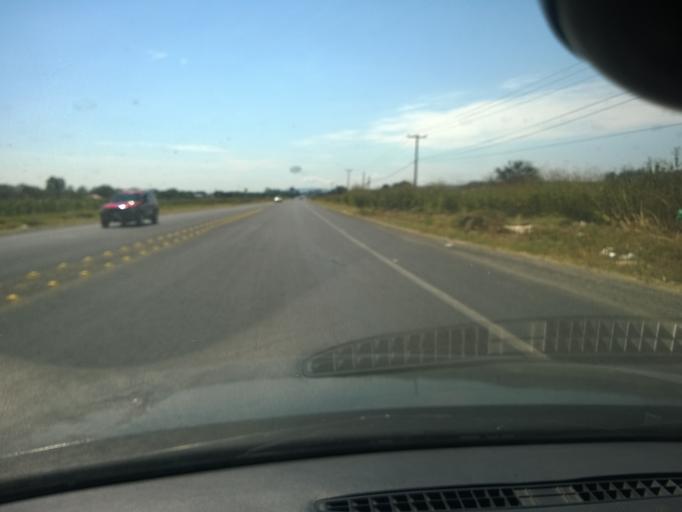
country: MX
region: Guanajuato
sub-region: Leon
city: El CERESO
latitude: 21.0173
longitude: -101.6991
